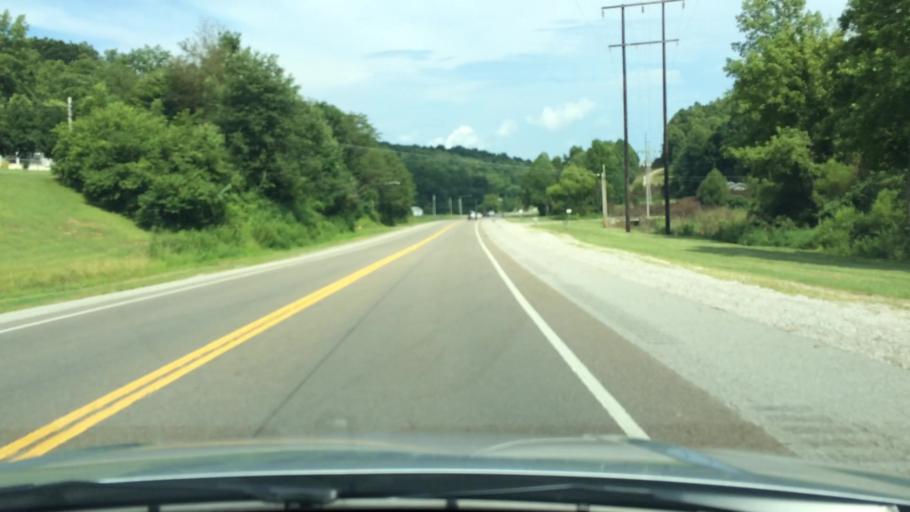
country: US
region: Tennessee
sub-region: Scott County
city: Huntsville
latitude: 36.4148
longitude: -84.4698
